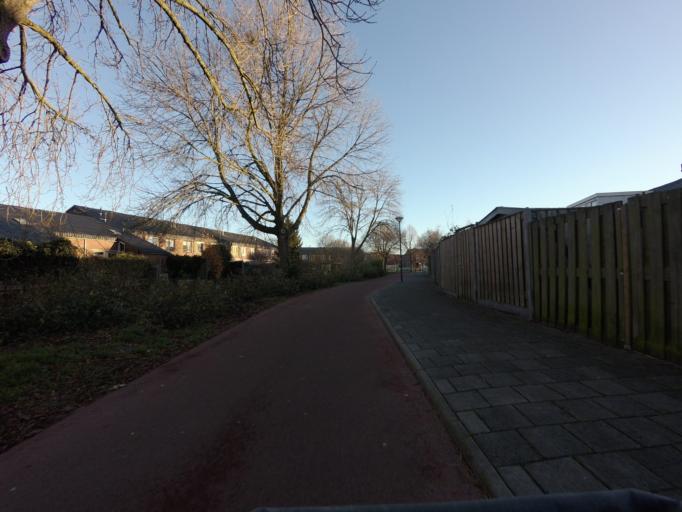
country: NL
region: Utrecht
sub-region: Stichtse Vecht
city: Spechtenkamp
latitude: 52.1425
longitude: 5.0167
